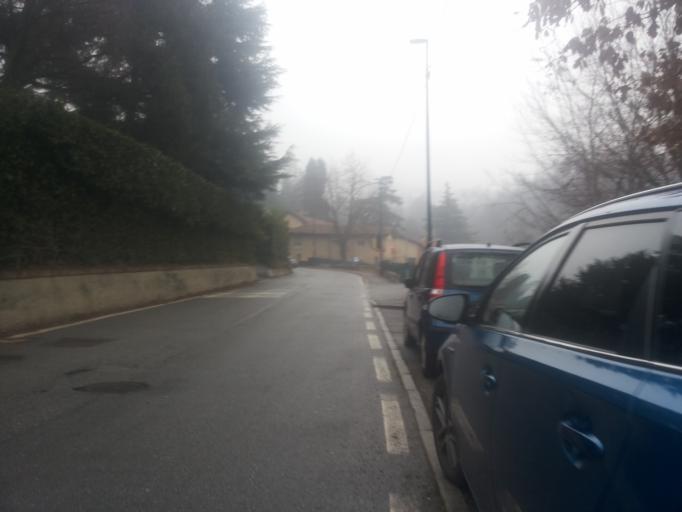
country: IT
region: Piedmont
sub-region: Provincia di Torino
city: Turin
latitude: 45.0513
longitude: 7.7145
